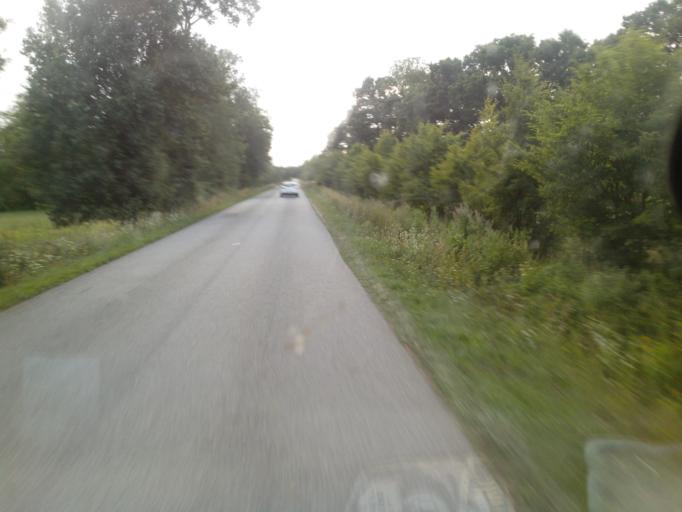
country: FR
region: Brittany
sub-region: Departement du Morbihan
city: Mauron
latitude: 48.0692
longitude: -2.2315
